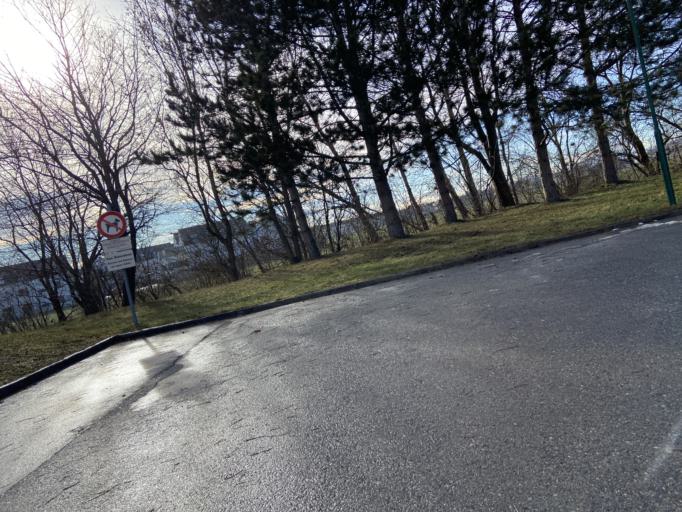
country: AT
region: Lower Austria
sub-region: Politischer Bezirk Modling
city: Laxenburg
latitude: 48.0681
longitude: 16.3516
